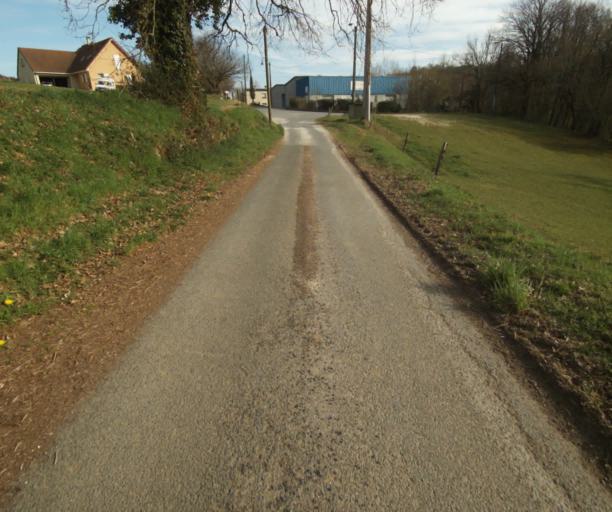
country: FR
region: Limousin
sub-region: Departement de la Correze
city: Tulle
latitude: 45.2899
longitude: 1.7607
